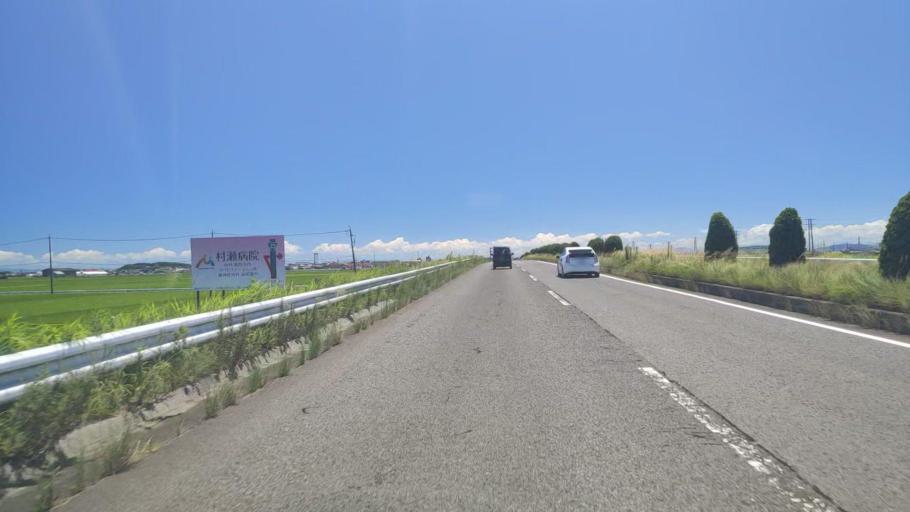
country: JP
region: Mie
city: Suzuka
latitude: 34.8824
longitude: 136.5974
